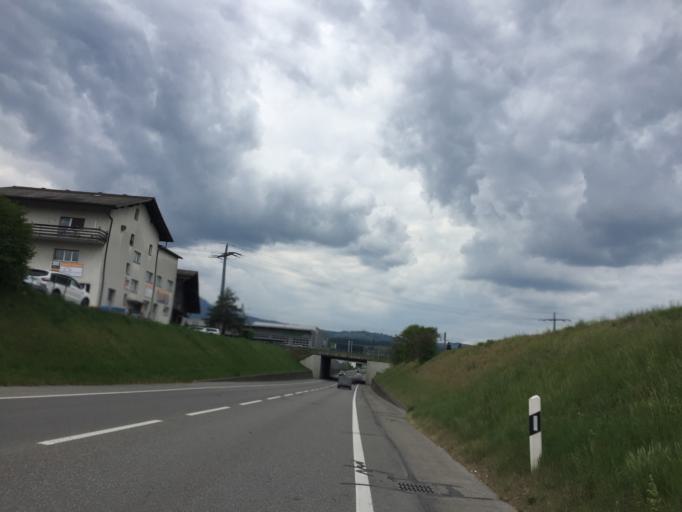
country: CH
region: Bern
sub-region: Thun District
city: Heimberg
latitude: 46.7805
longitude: 7.5918
